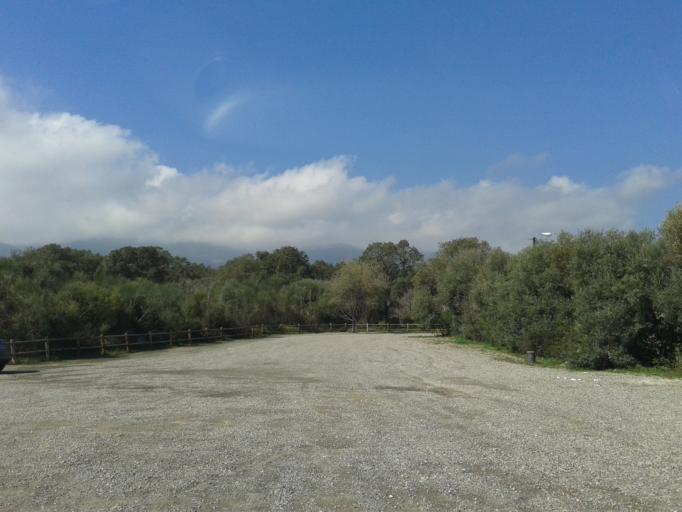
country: FR
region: Corsica
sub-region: Departement de la Haute-Corse
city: Biguglia
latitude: 42.6437
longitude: 9.4436
